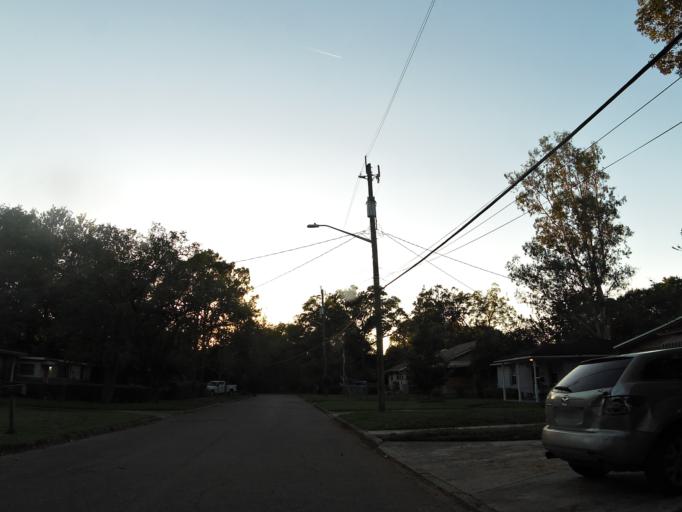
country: US
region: Florida
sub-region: Duval County
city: Jacksonville
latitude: 30.3159
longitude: -81.7148
